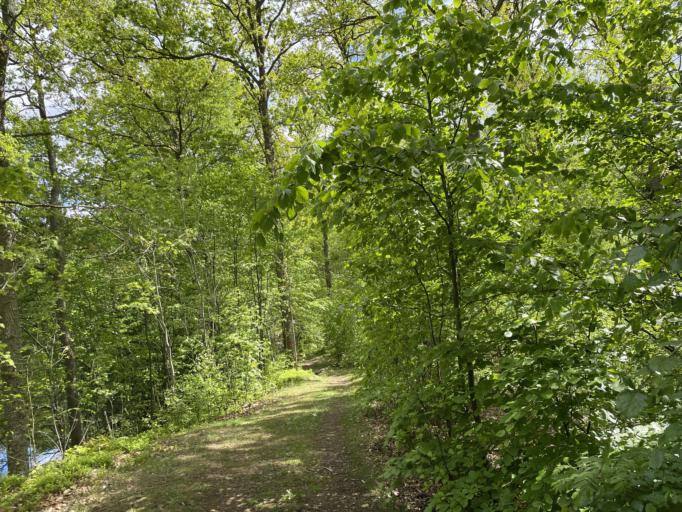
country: SE
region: Skane
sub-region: Klippans Kommun
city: Klippan
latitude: 56.1605
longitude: 13.1491
